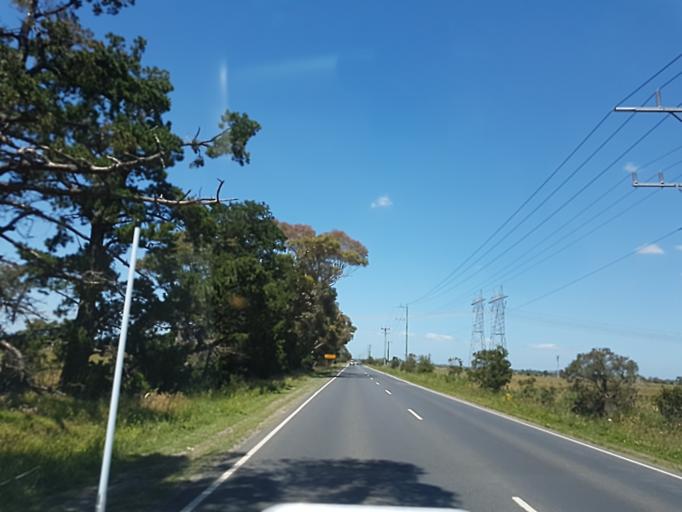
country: AU
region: Victoria
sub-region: Cardinia
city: Pakenham South
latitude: -38.1066
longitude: 145.4871
